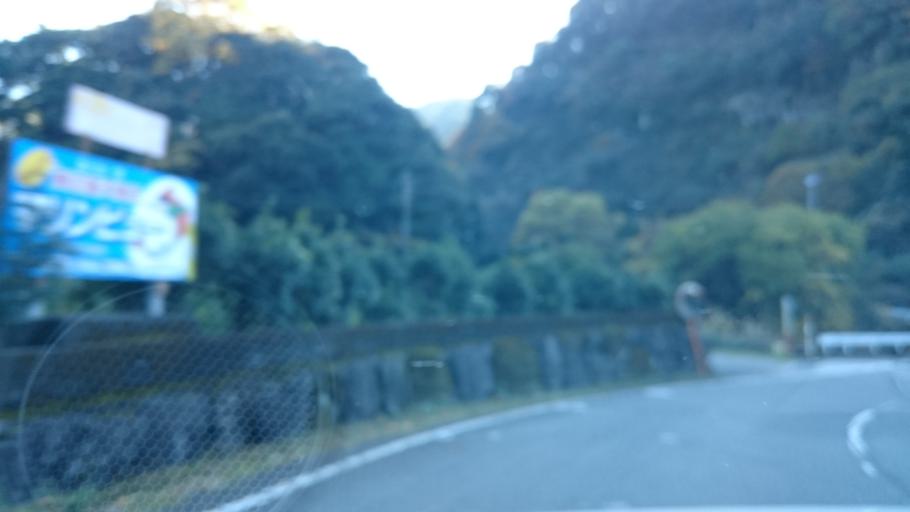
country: JP
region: Shizuoka
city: Heda
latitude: 34.9644
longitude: 138.8098
